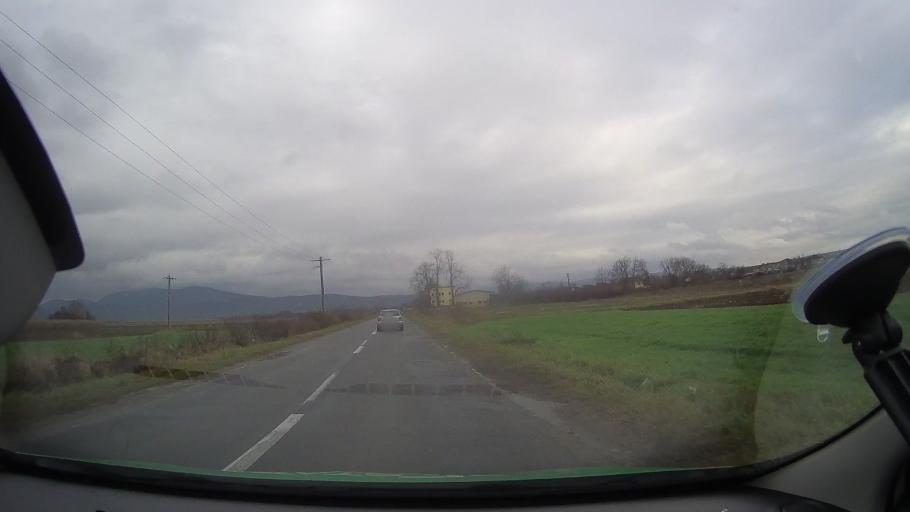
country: RO
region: Arad
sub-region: Comuna Buteni
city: Buteni
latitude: 46.3375
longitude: 22.1271
